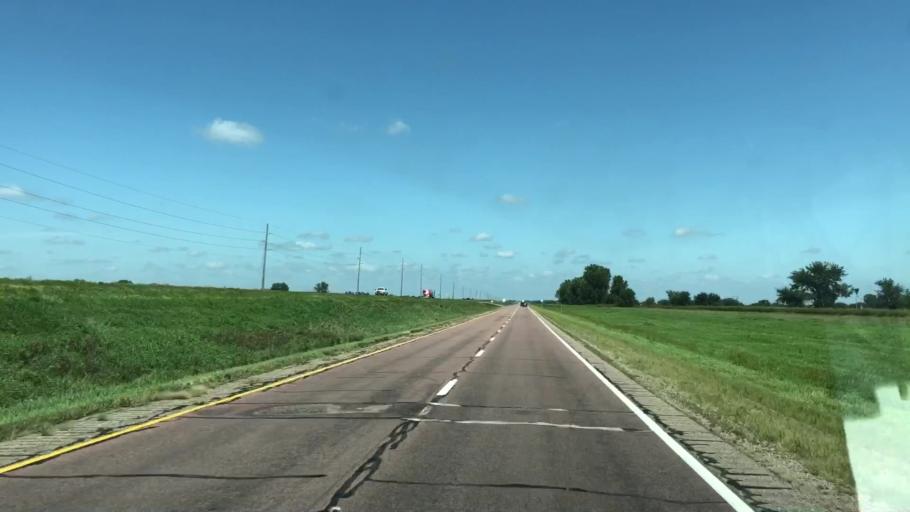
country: US
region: Iowa
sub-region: Plymouth County
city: Le Mars
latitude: 42.6746
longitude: -96.2717
